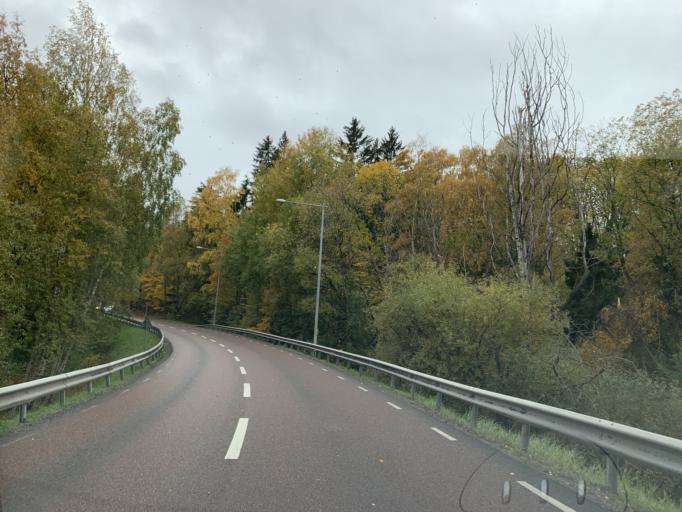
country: SE
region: Stockholm
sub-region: Botkyrka Kommun
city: Tumba
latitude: 59.1873
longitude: 17.8177
